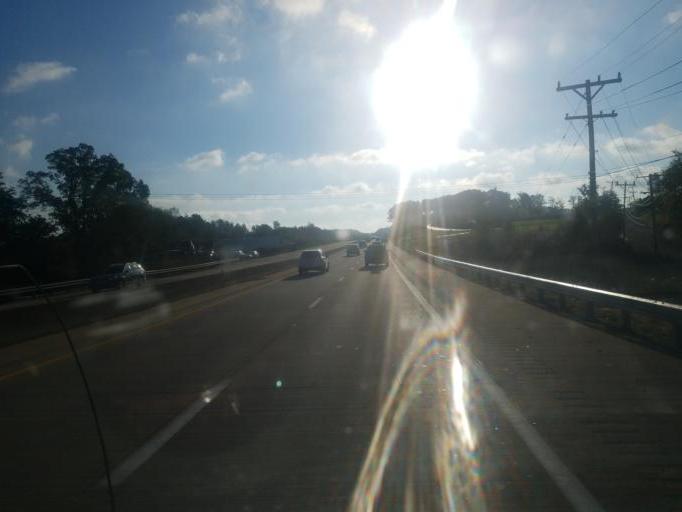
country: US
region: Pennsylvania
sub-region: Westmoreland County
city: Delmont
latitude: 40.4082
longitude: -79.6129
